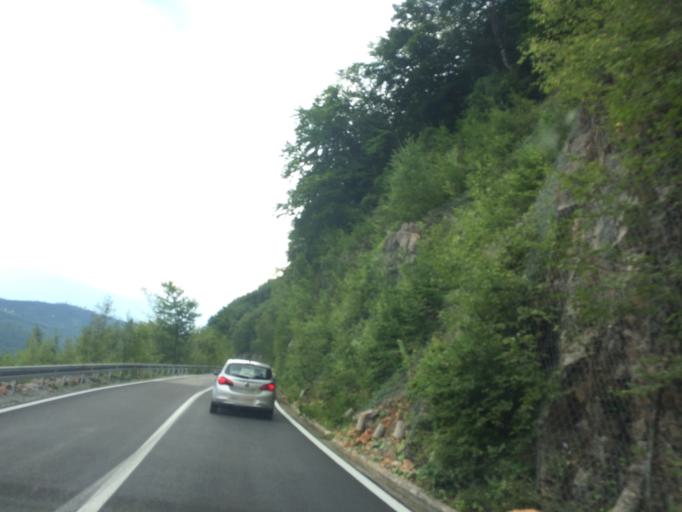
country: ME
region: Opstina Zabljak
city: Zabljak
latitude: 43.1515
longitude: 19.2778
